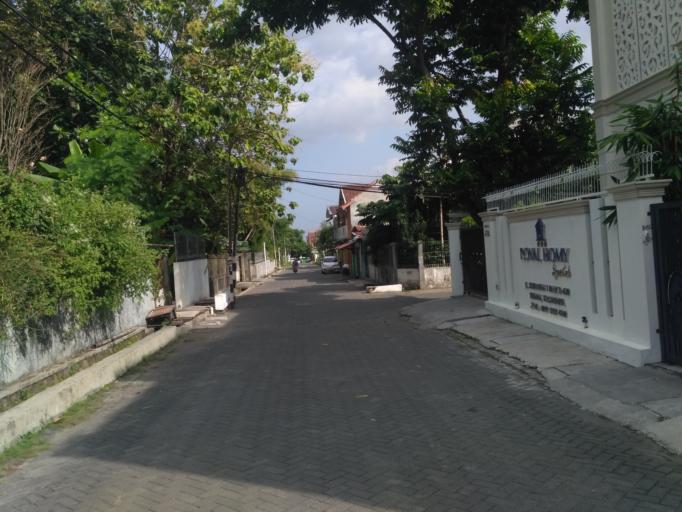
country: ID
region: Daerah Istimewa Yogyakarta
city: Depok
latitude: -7.7789
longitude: 110.4114
